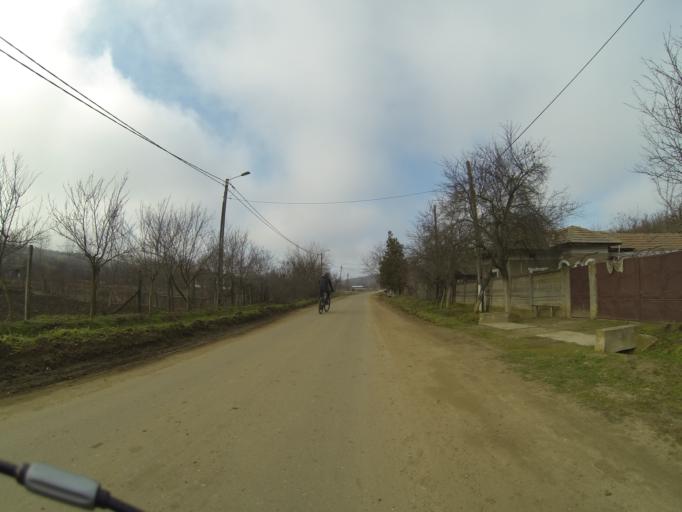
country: RO
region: Mehedinti
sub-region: Comuna Poroina Mare
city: Poroina Mare
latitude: 44.4925
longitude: 22.9997
